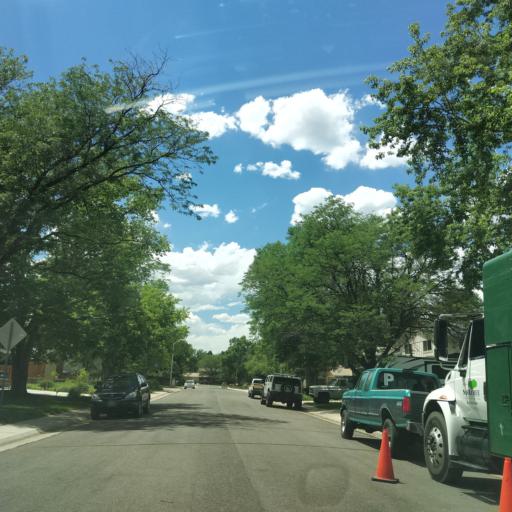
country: US
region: Colorado
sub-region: Jefferson County
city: Lakewood
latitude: 39.6871
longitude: -105.1018
